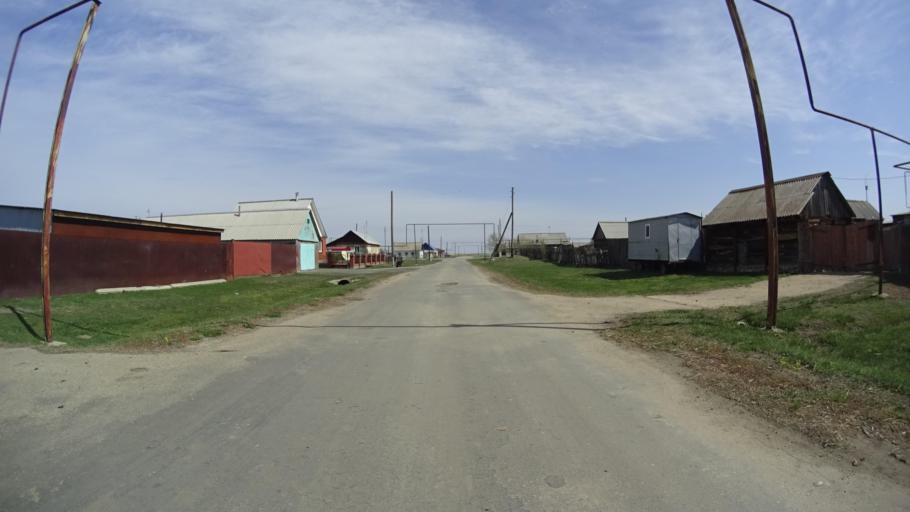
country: RU
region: Chelyabinsk
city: Chesma
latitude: 53.7990
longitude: 61.0202
